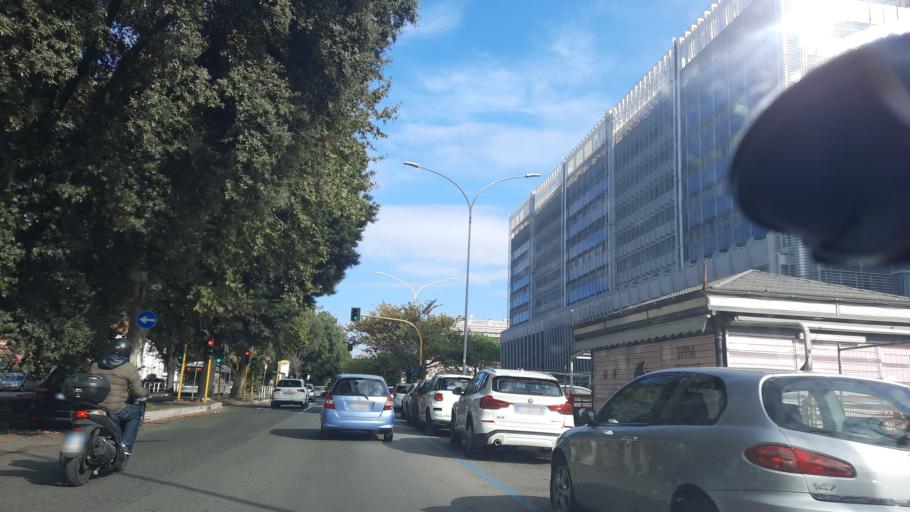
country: IT
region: Latium
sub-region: Citta metropolitana di Roma Capitale
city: Rome
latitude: 41.8649
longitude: 12.4791
